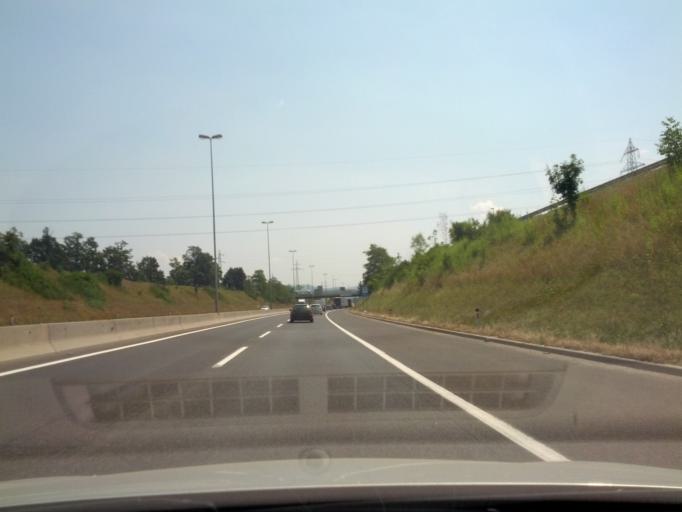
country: SI
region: Ljubljana
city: Ljubljana
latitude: 46.0775
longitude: 14.5371
